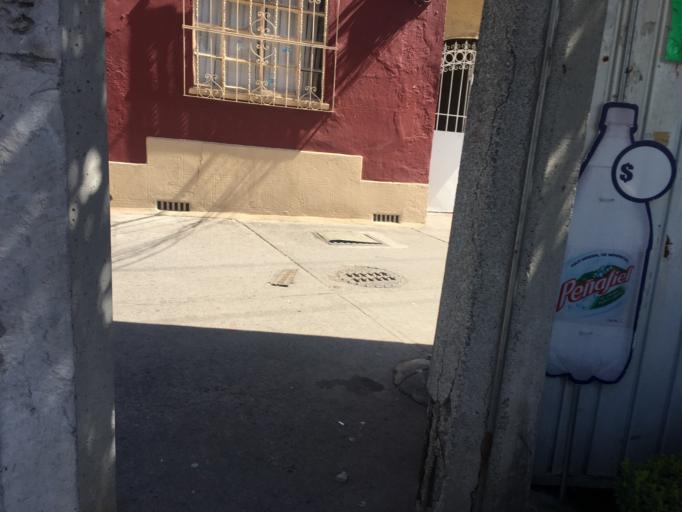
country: MX
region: Mexico City
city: Benito Juarez
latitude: 19.4070
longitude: -99.1569
